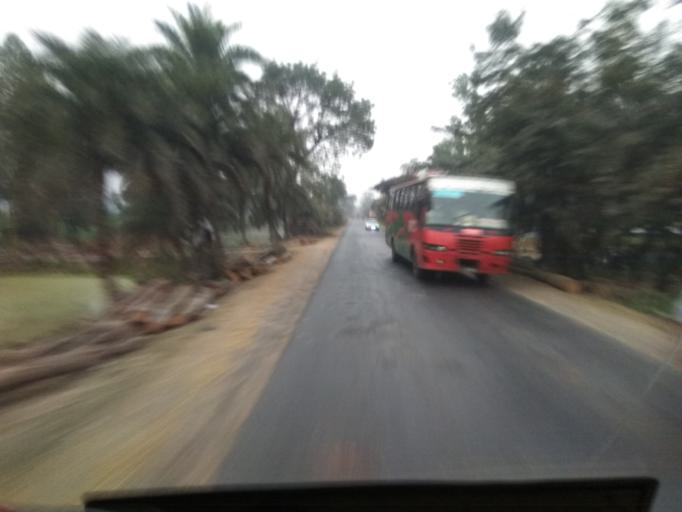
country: BD
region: Rajshahi
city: Bogra
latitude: 24.7377
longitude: 89.3303
